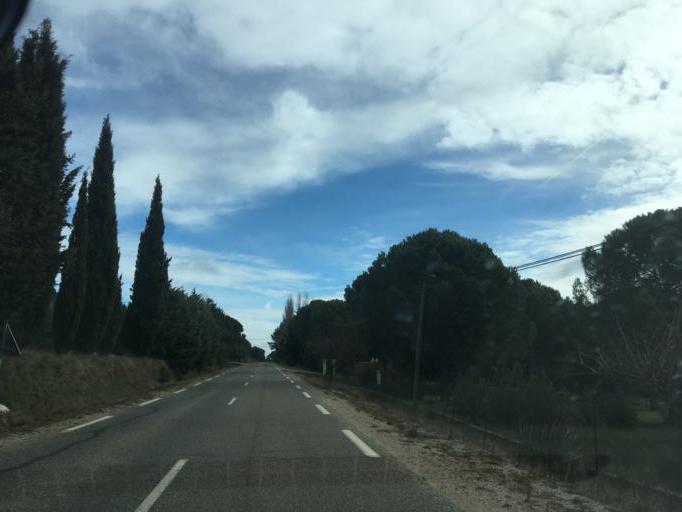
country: FR
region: Provence-Alpes-Cote d'Azur
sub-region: Departement du Var
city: La Celle
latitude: 43.4444
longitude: 6.0190
